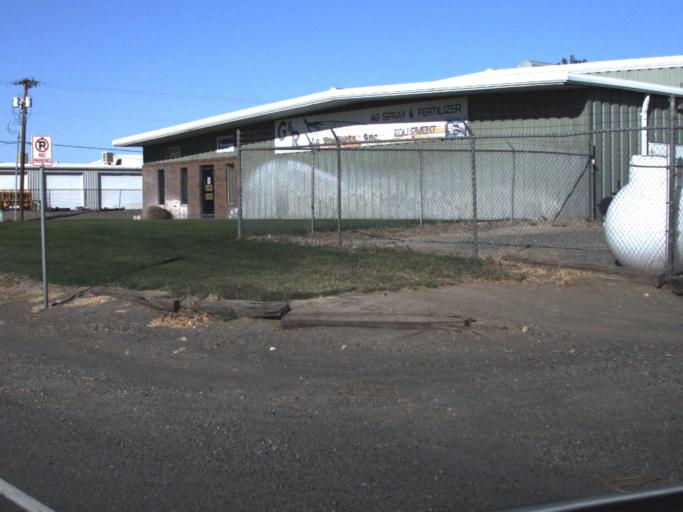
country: US
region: Washington
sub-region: Franklin County
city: Pasco
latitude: 46.2398
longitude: -119.0832
